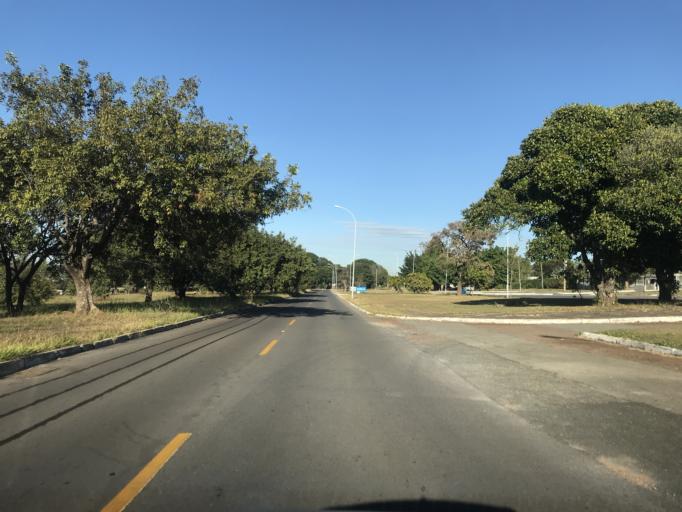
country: BR
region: Federal District
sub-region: Brasilia
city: Brasilia
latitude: -15.8182
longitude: -47.8848
